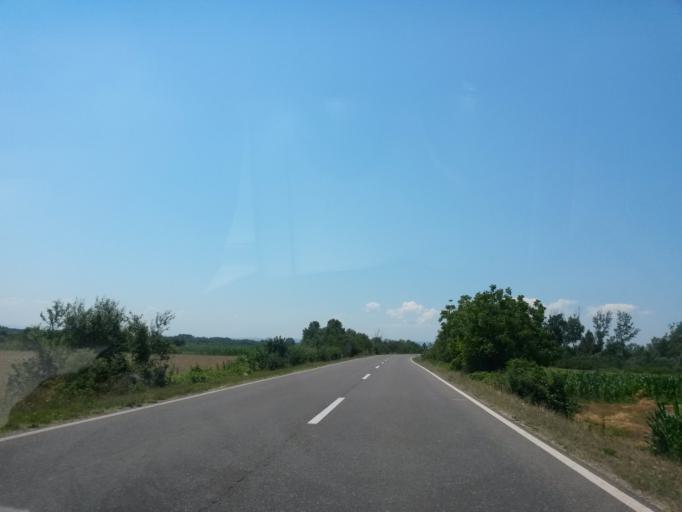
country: BA
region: Federation of Bosnia and Herzegovina
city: Donja Dubica
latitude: 45.0129
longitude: 18.3987
